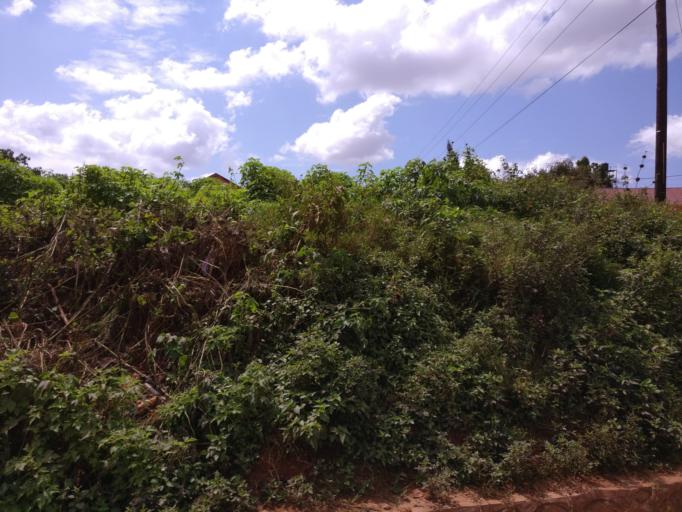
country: UG
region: Central Region
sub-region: Kampala District
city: Kampala
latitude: 0.2845
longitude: 32.5630
